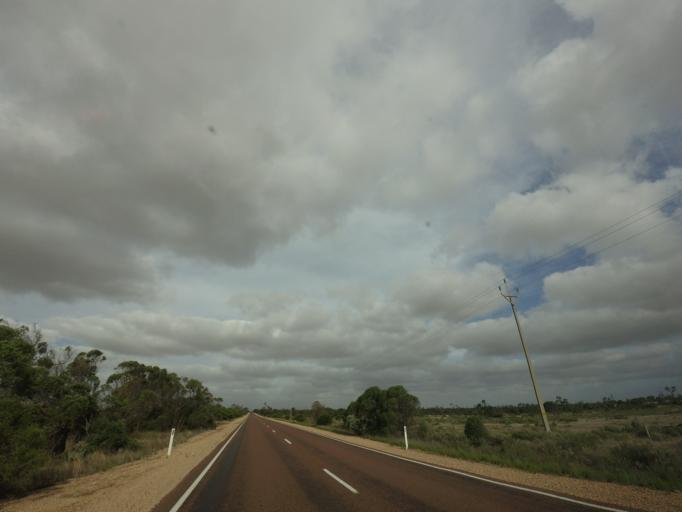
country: AU
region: South Australia
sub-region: Ceduna
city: Ceduna
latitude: -31.9409
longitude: 133.2348
